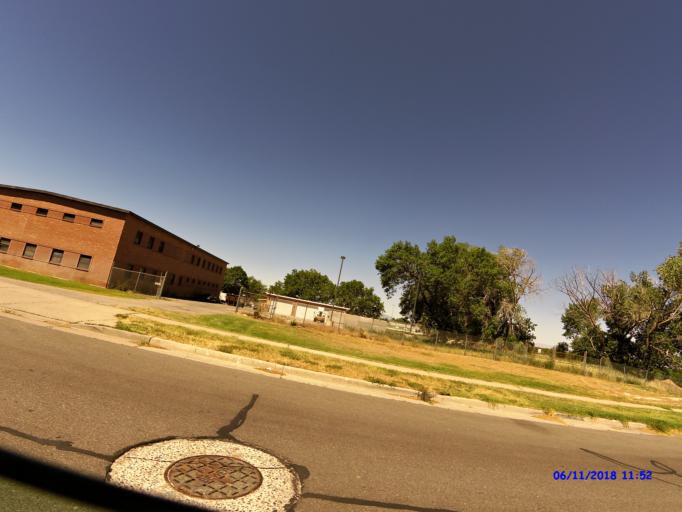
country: US
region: Utah
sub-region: Weber County
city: Ogden
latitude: 41.2332
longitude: -111.9535
